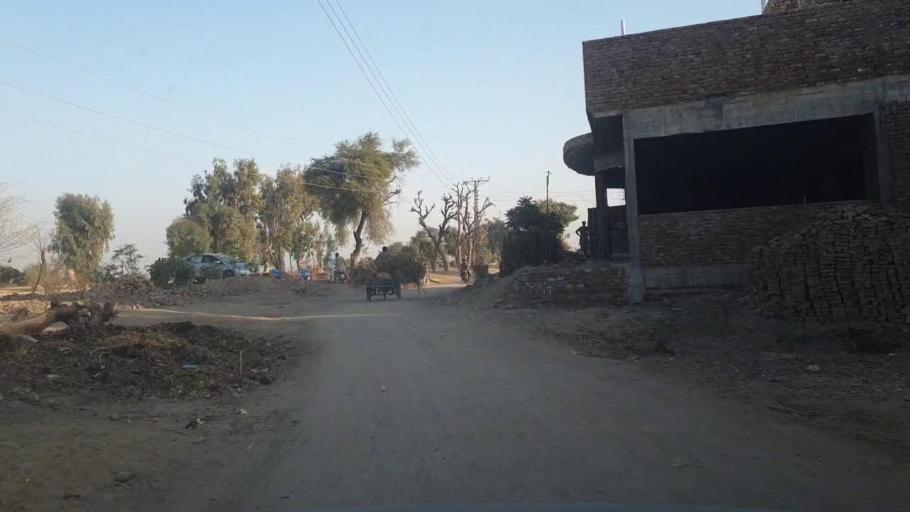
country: PK
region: Sindh
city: Chambar
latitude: 25.2947
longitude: 68.8924
